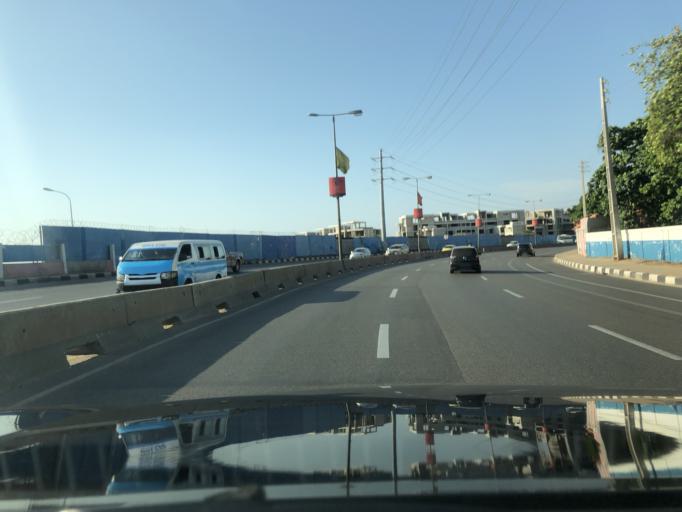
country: AO
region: Luanda
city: Luanda
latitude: -8.8994
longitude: 13.1769
